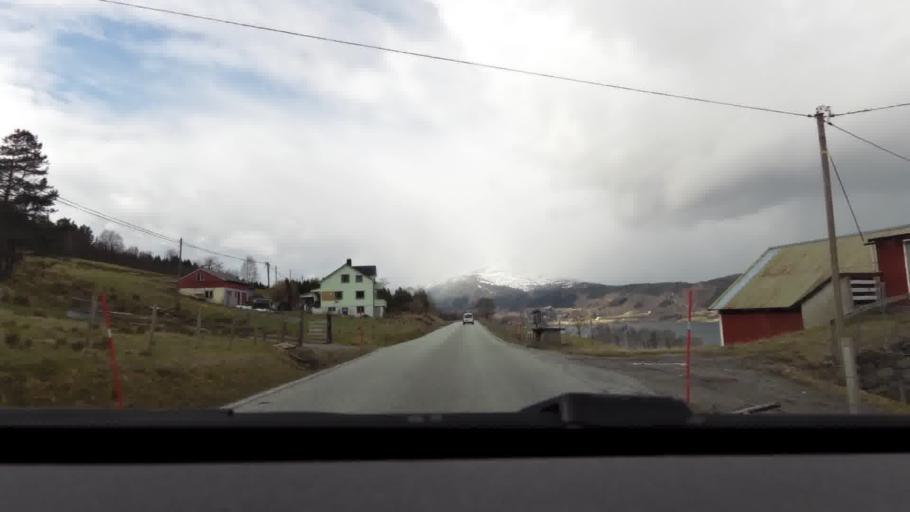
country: NO
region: More og Romsdal
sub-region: Averoy
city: Bruhagen
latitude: 63.1095
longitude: 7.6347
